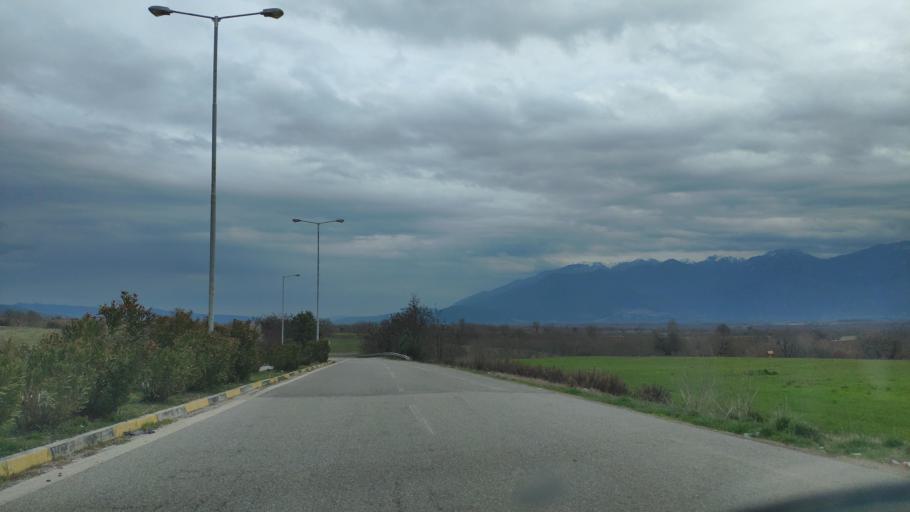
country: GR
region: Central Greece
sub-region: Nomos Fthiotidos
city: Anthili
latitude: 38.7120
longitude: 22.4626
